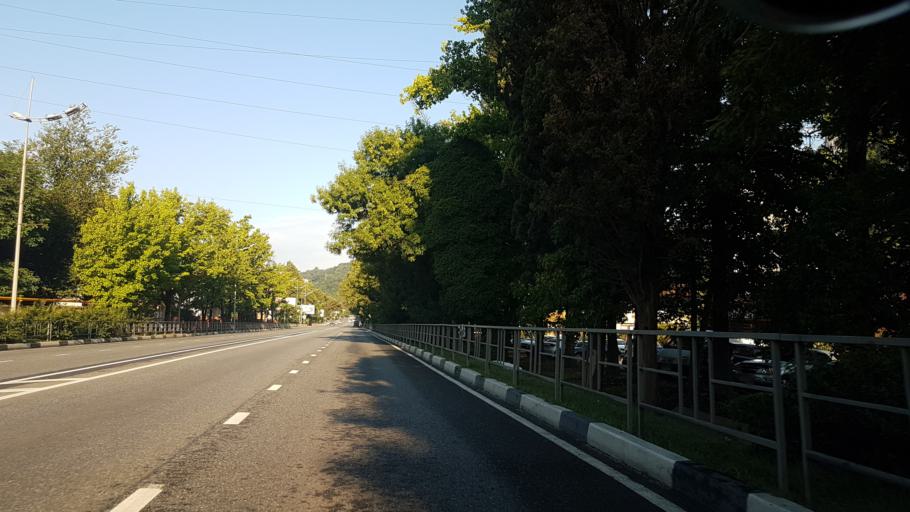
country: RU
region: Krasnodarskiy
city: Dagomys
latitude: 43.6616
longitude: 39.6667
